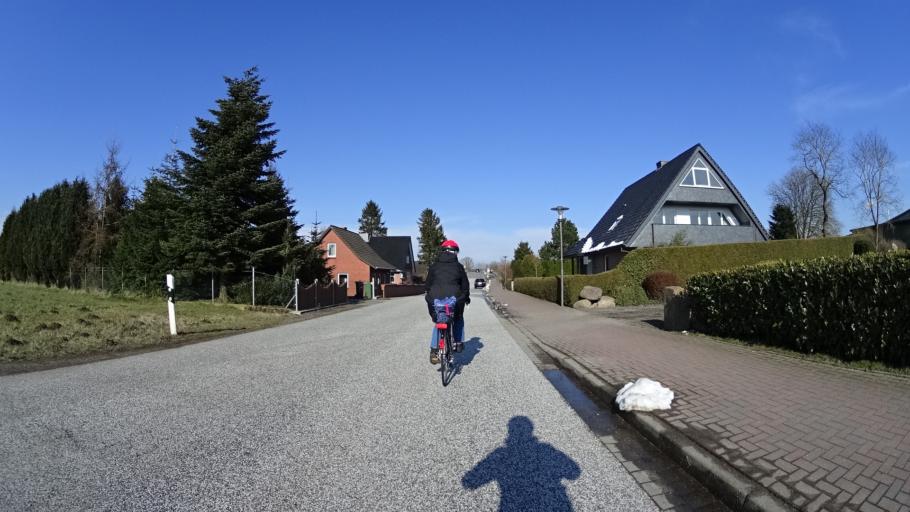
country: DE
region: Schleswig-Holstein
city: Schellhorn
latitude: 54.2438
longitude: 10.3009
